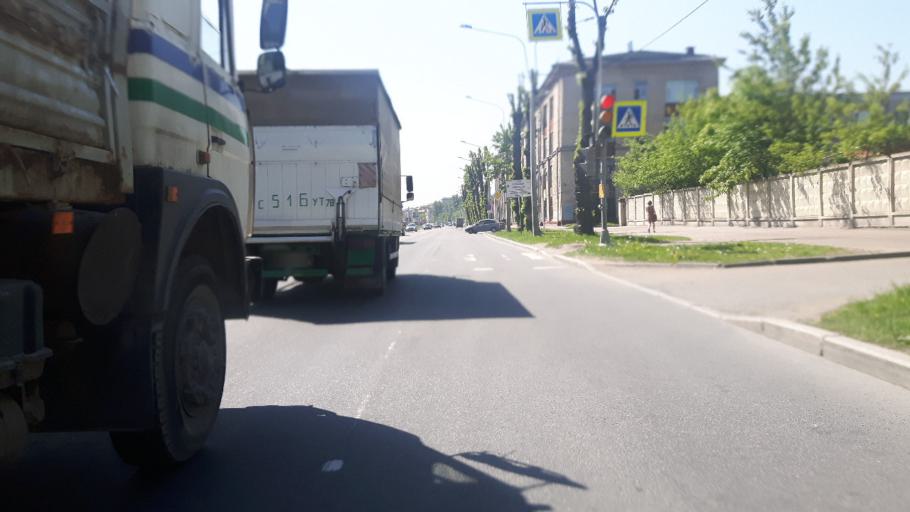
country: RU
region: St.-Petersburg
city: Admiralteisky
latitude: 59.8951
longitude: 30.2852
